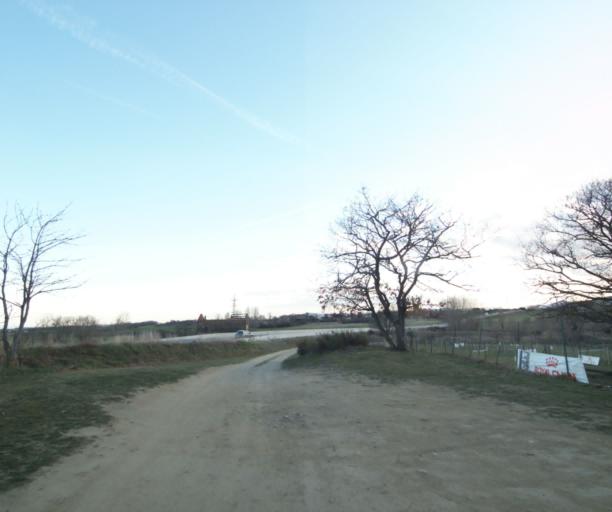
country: FR
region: Rhone-Alpes
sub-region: Departement de l'Ardeche
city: Davezieux
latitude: 45.2491
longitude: 4.7160
